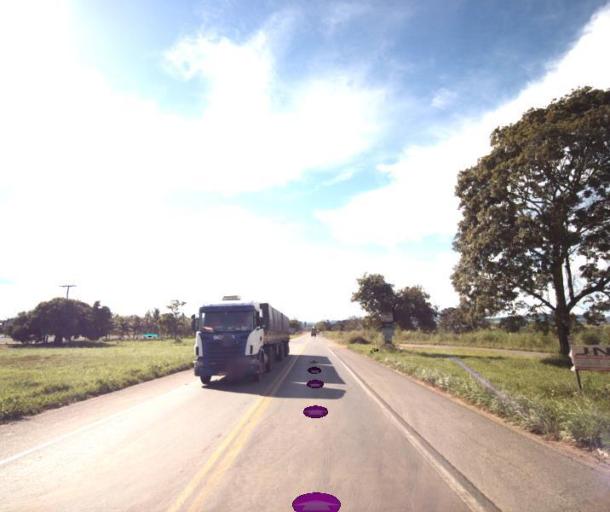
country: BR
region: Goias
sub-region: Rialma
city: Rialma
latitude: -15.4743
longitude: -49.4960
